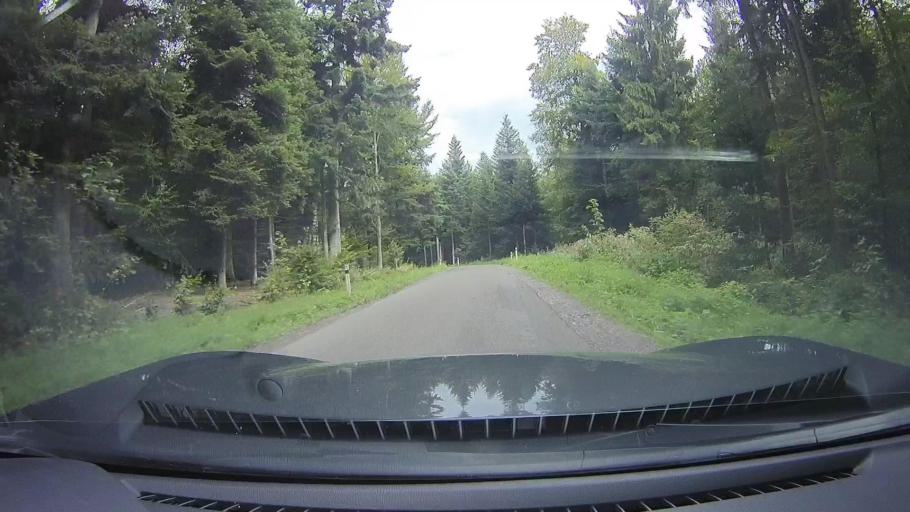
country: DE
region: Baden-Wuerttemberg
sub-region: Regierungsbezirk Stuttgart
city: Althutte
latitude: 48.9303
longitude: 9.5922
